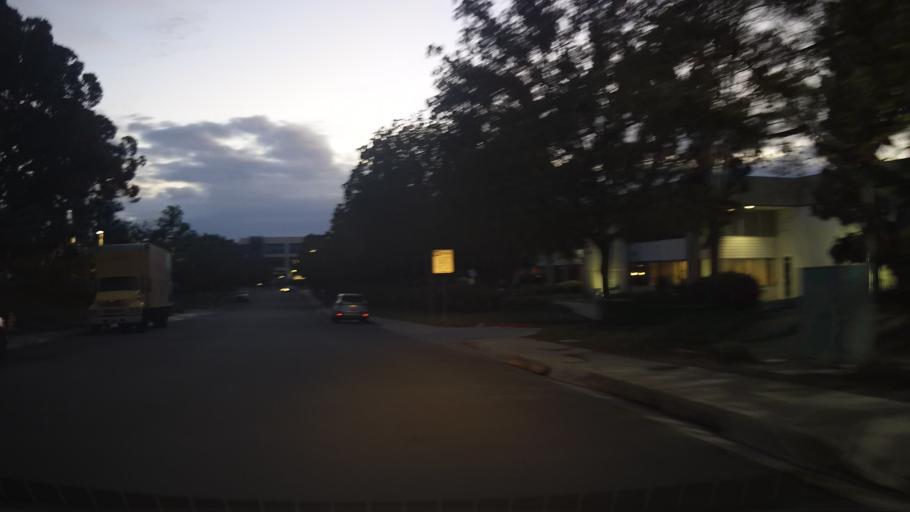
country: US
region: California
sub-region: San Diego County
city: National City
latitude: 32.7150
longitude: -117.1135
